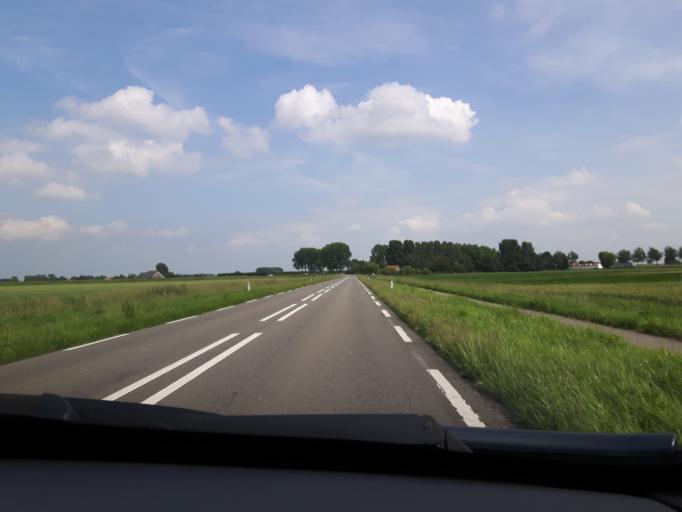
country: NL
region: Zeeland
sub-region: Gemeente Noord-Beveland
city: Kamperland
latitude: 51.4992
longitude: 3.7255
